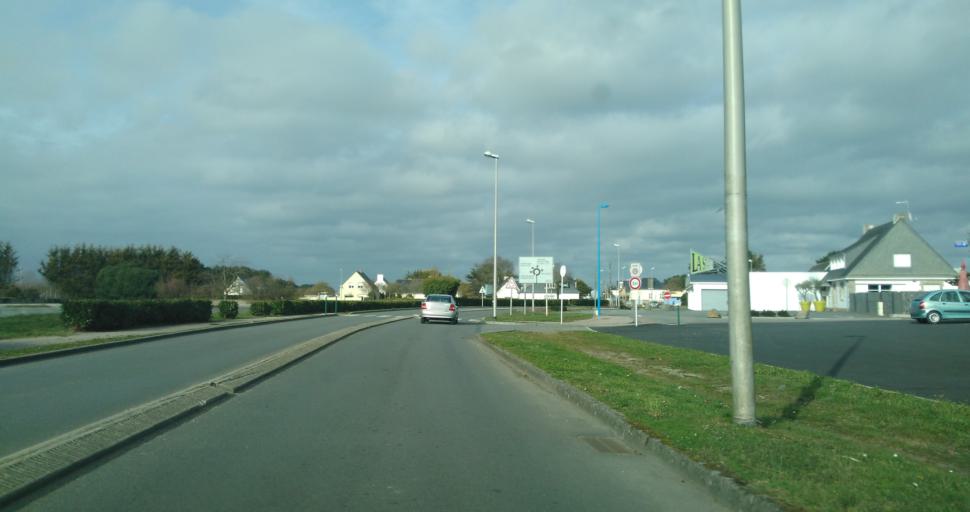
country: FR
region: Brittany
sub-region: Departement du Morbihan
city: Penestin
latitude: 47.4771
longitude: -2.4792
